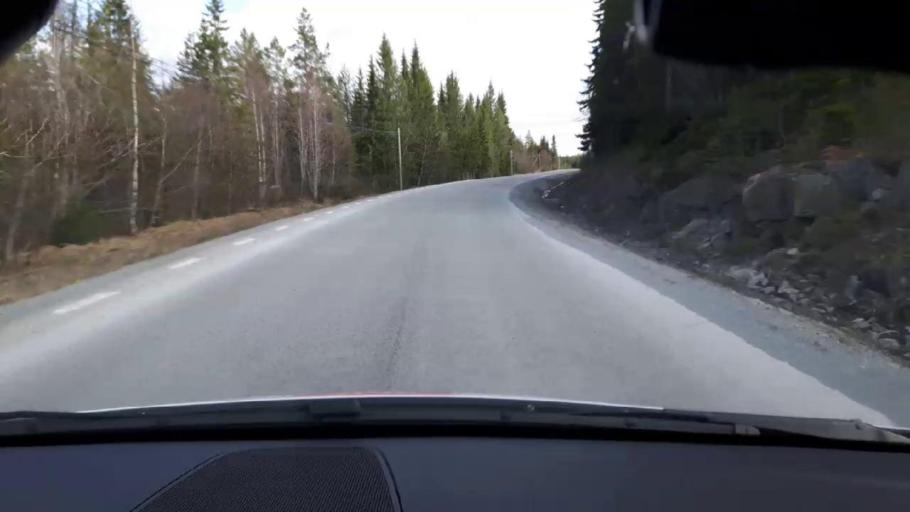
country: SE
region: Jaemtland
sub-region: Bergs Kommun
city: Hoverberg
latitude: 62.7416
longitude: 14.5841
